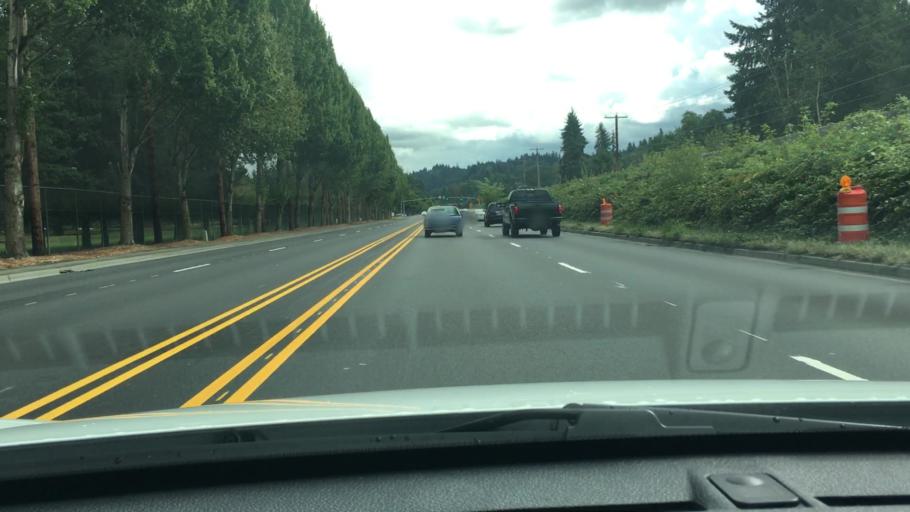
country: US
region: Washington
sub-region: King County
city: Fairwood
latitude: 47.4724
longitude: -122.1671
